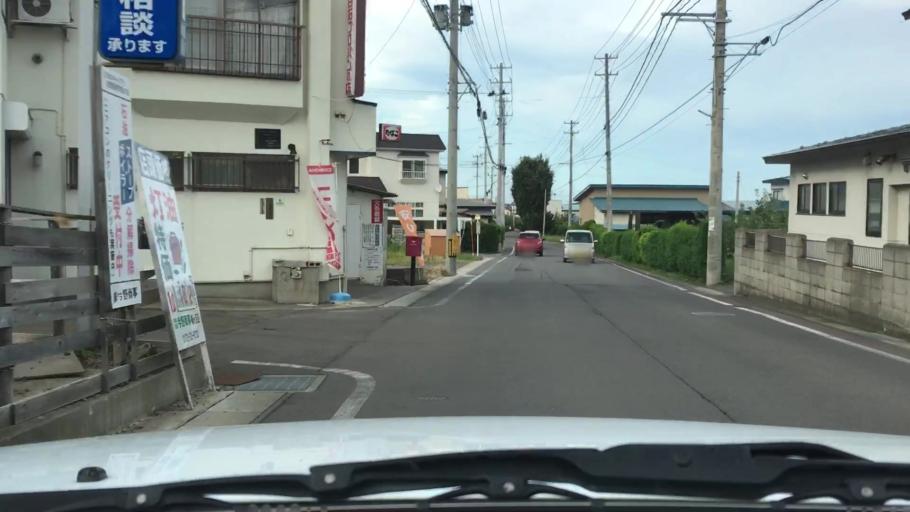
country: JP
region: Aomori
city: Hirosaki
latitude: 40.5840
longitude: 140.4601
